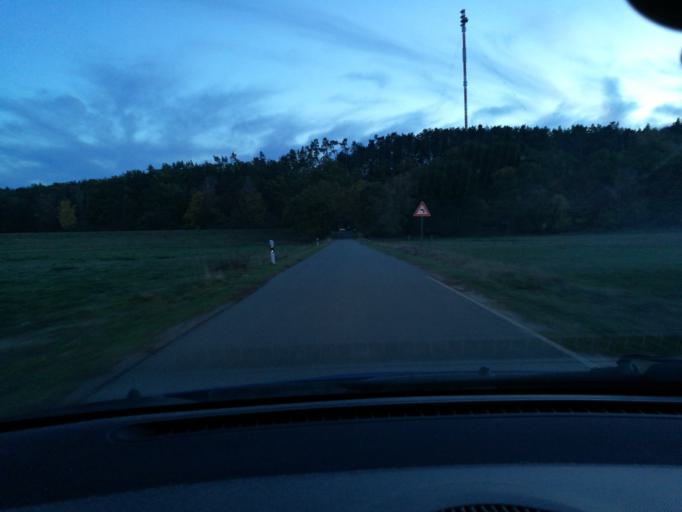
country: DE
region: Brandenburg
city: Lenzen
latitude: 53.0735
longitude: 11.4499
